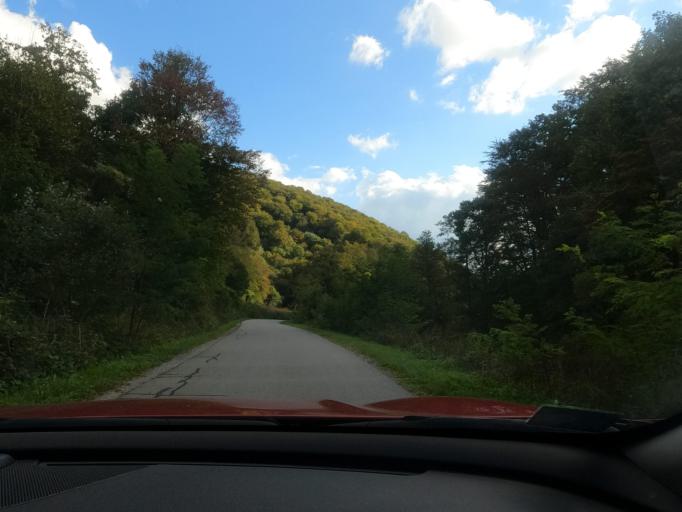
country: HR
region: Sisacko-Moslavacka
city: Petrinja
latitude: 45.4033
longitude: 16.2467
